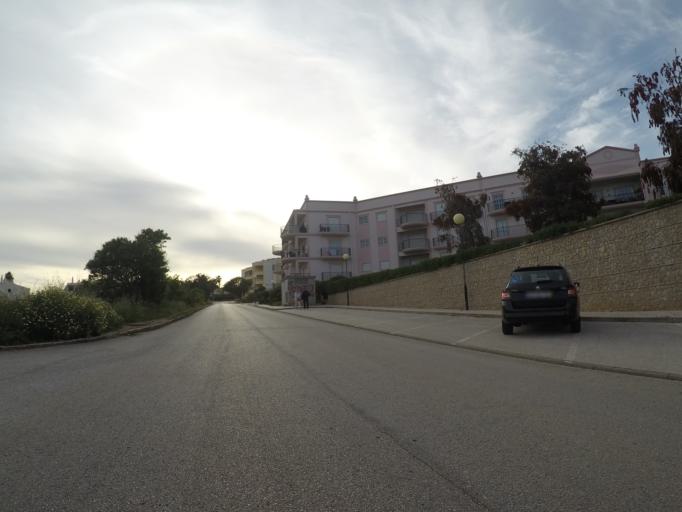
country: PT
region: Faro
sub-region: Lagos
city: Lagos
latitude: 37.0868
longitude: -8.7354
